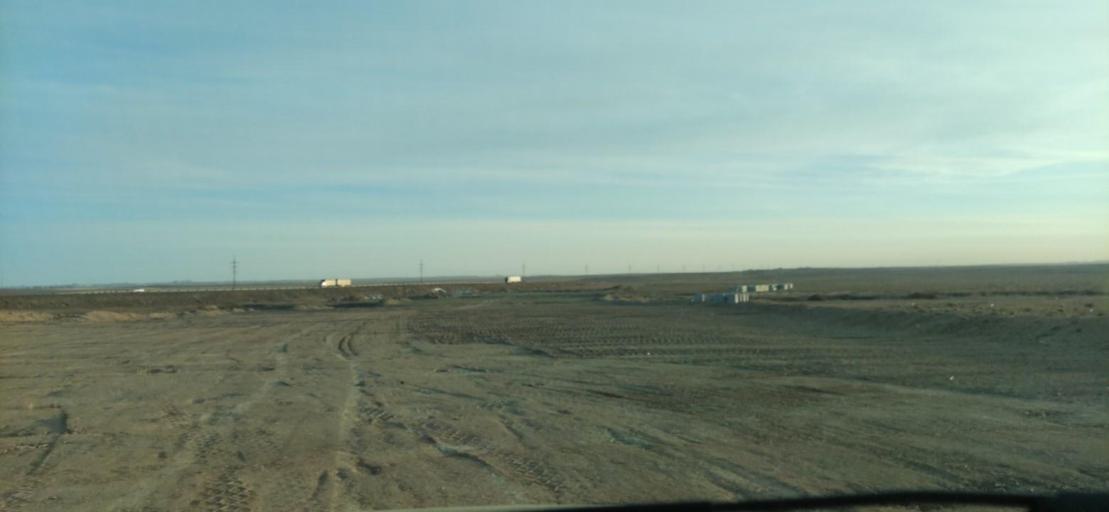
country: KZ
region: Qaraghandy
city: Saryshaghan
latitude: 46.0939
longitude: 73.6049
